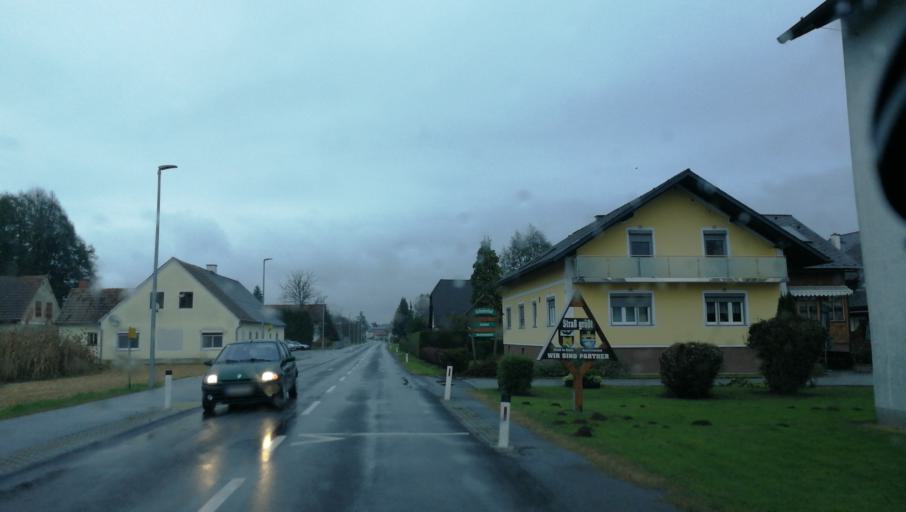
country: AT
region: Styria
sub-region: Politischer Bezirk Leibnitz
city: Spielfeld
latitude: 46.7124
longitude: 15.6385
